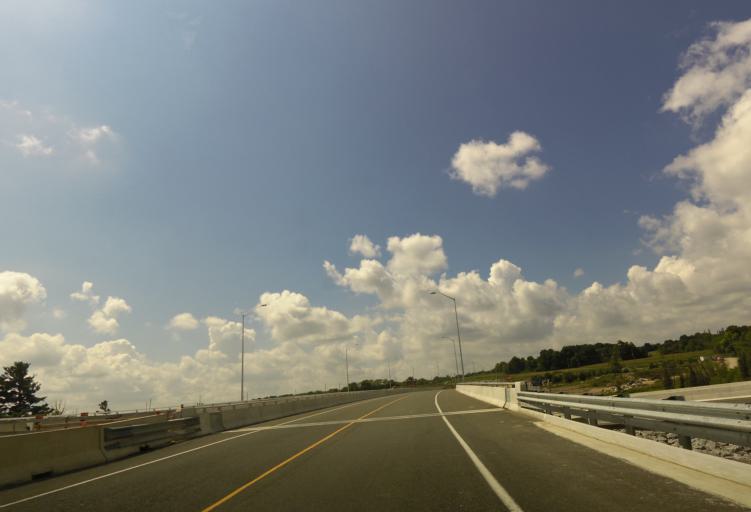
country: CA
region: Ontario
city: Pickering
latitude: 43.9228
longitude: -79.0917
